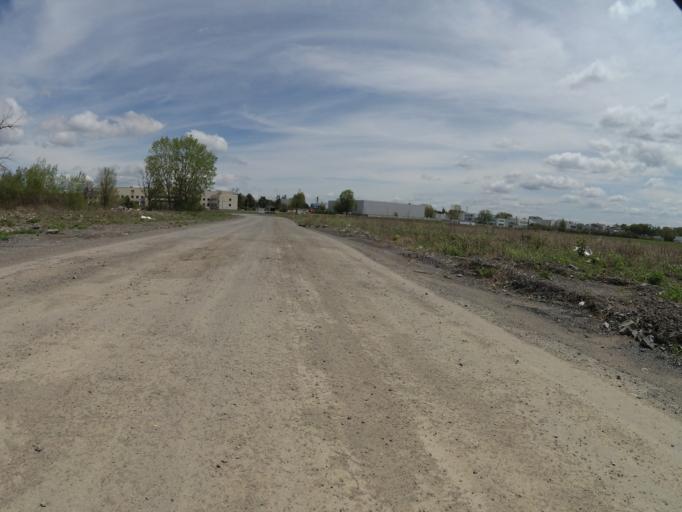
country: CA
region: Quebec
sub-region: Outaouais
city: Gatineau
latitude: 45.4530
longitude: -75.6286
